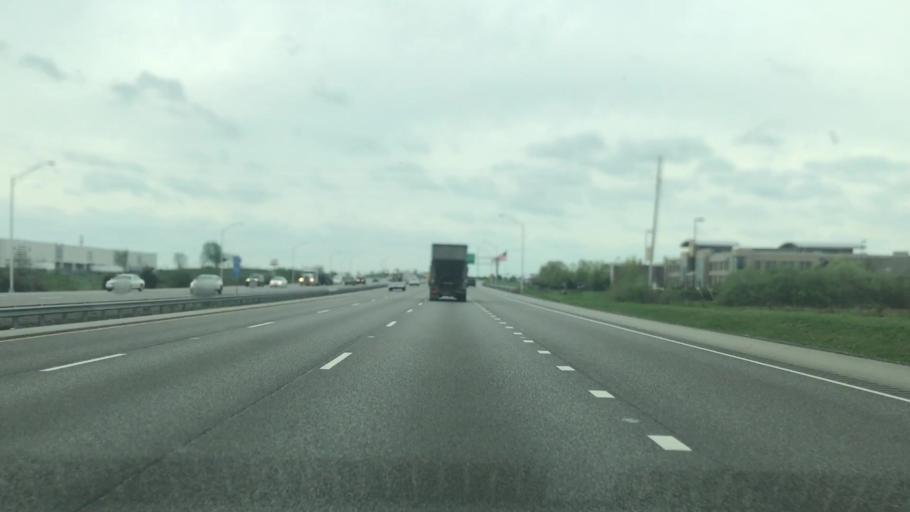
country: US
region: Indiana
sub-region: Johnson County
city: Greenwood
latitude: 39.6215
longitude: -86.0747
